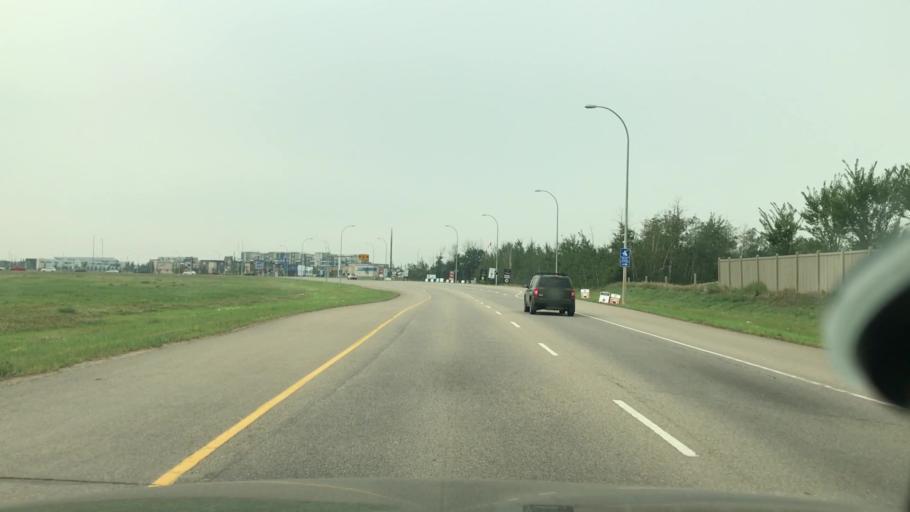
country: CA
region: Alberta
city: Devon
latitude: 53.4400
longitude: -113.6110
